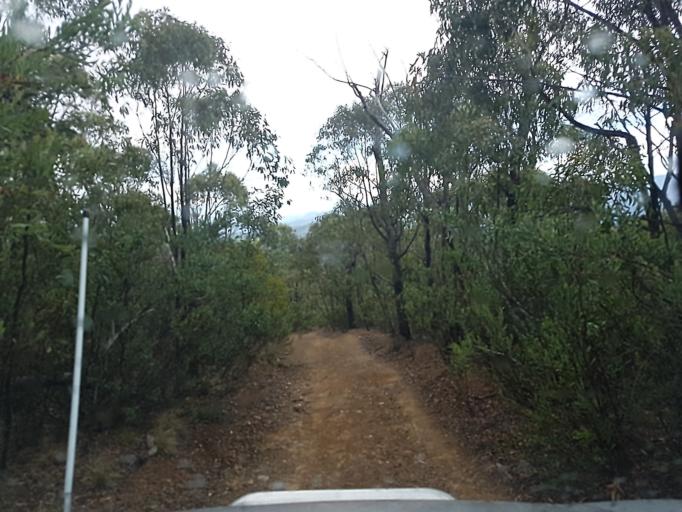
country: AU
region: New South Wales
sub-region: Snowy River
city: Jindabyne
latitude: -36.9135
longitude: 148.3358
